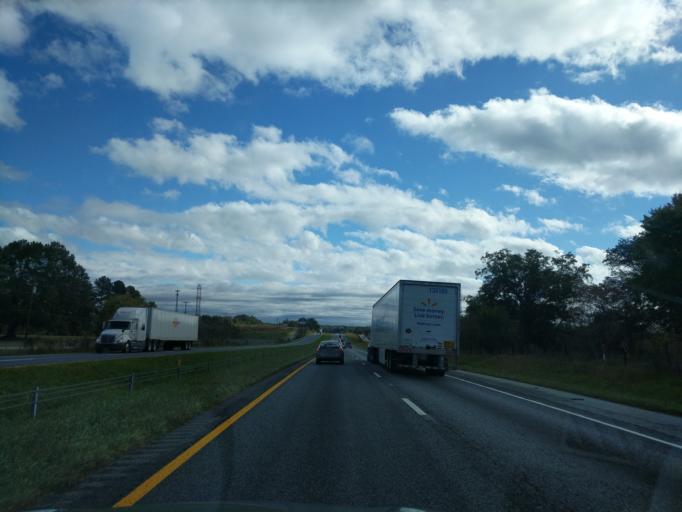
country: US
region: South Carolina
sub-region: Spartanburg County
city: Cowpens
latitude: 35.0731
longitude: -81.7549
